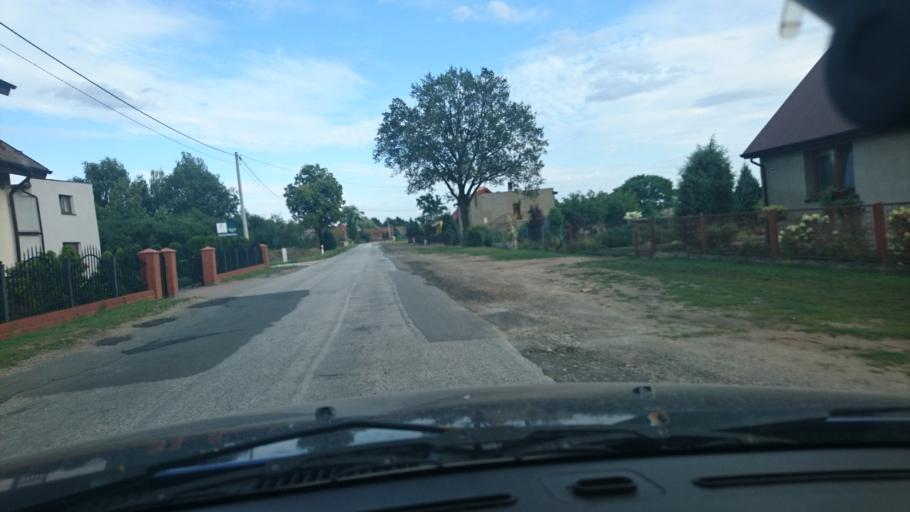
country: PL
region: Greater Poland Voivodeship
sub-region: Powiat ostrzeszowski
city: Kobyla Gora
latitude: 51.4824
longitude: 17.7916
